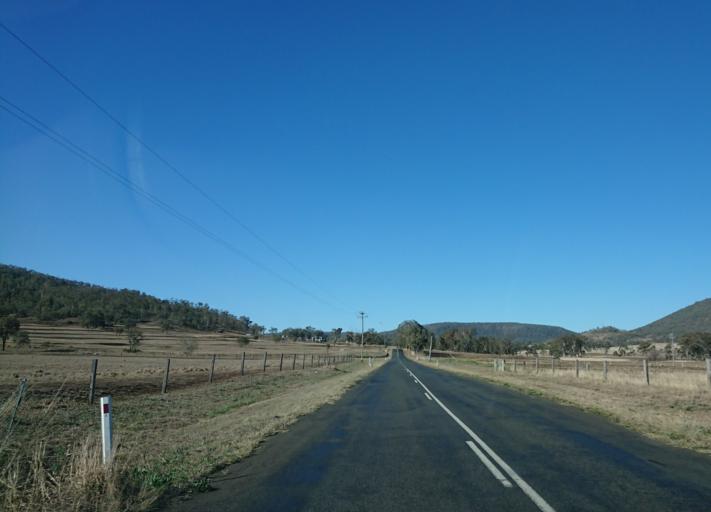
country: AU
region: Queensland
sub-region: Toowoomba
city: Top Camp
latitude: -27.8383
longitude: 152.0748
